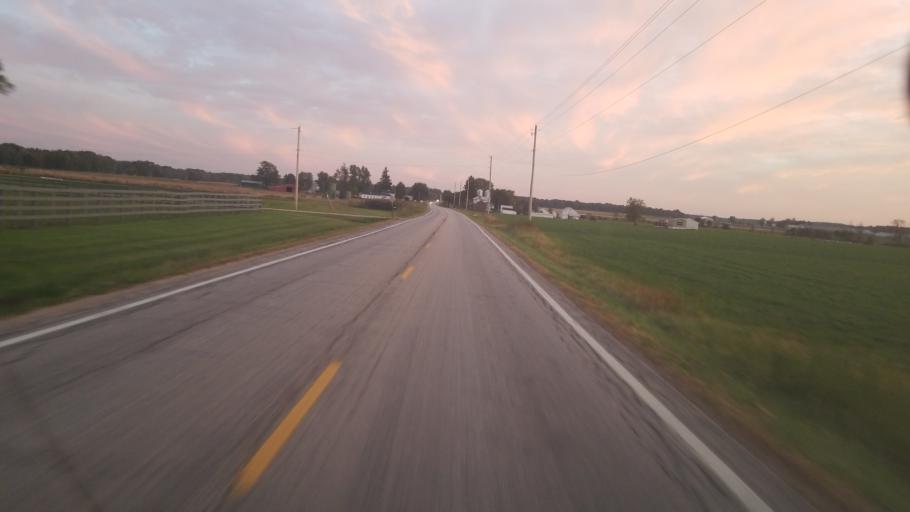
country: US
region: Ohio
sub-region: Ashtabula County
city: Andover
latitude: 41.6705
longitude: -80.6677
